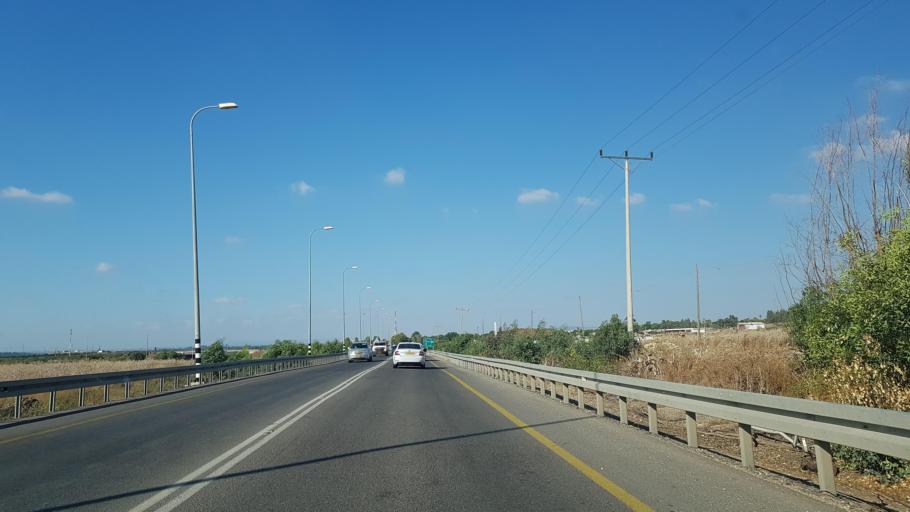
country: PS
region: West Bank
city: Tulkarm
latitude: 32.3409
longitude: 35.0104
